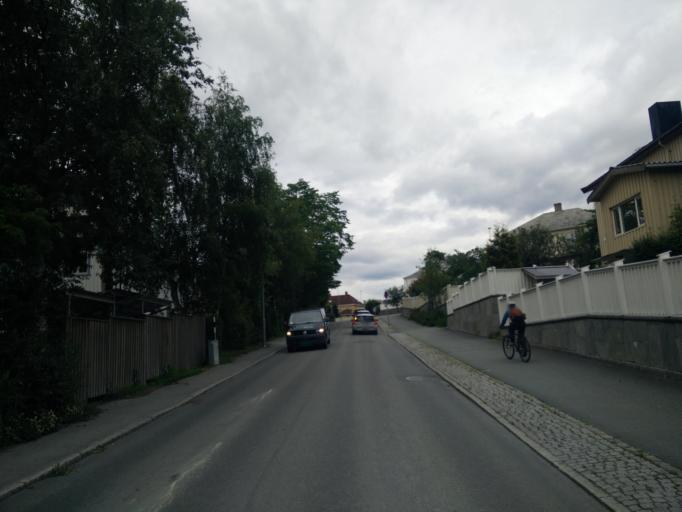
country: NO
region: Sor-Trondelag
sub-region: Trondheim
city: Trondheim
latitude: 63.4178
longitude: 10.4125
